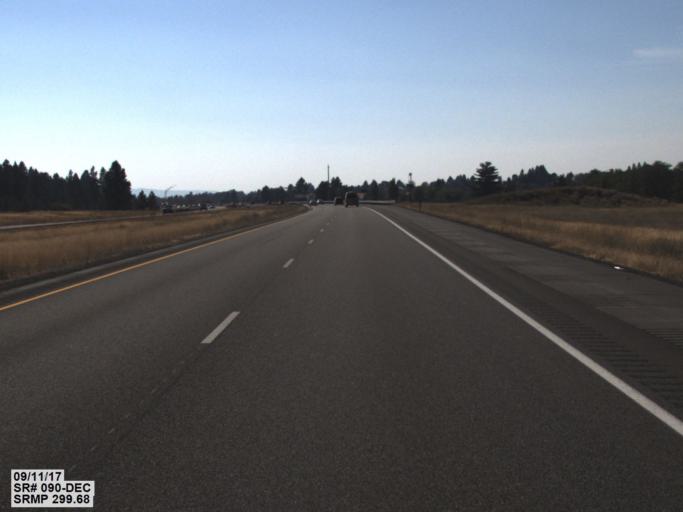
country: US
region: Washington
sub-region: Spokane County
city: Otis Orchards-East Farms
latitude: 47.6965
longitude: -117.0447
